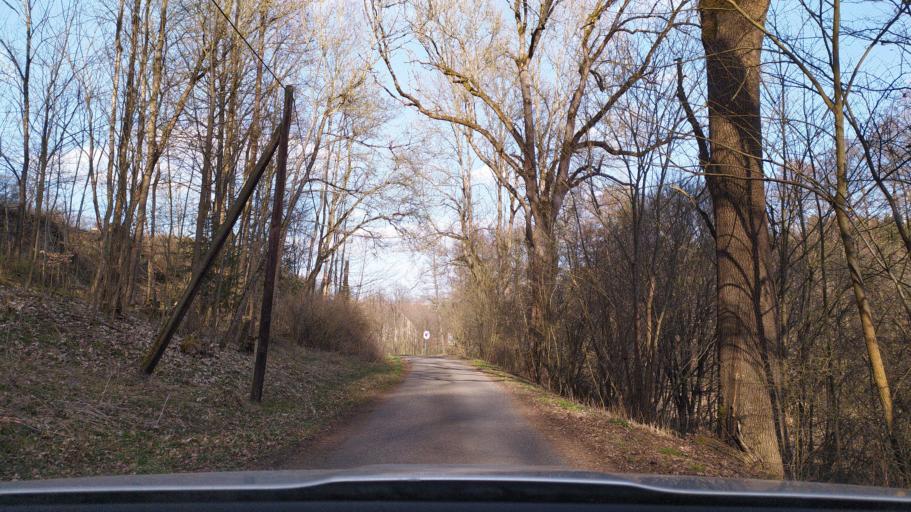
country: DE
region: Bavaria
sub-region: Upper Franconia
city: Hohenberg an der Eger
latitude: 50.1204
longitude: 12.2313
